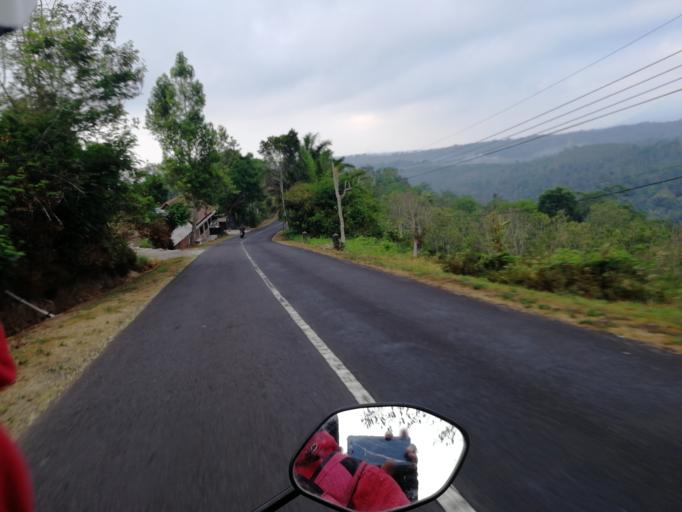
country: ID
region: Bali
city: Banjar Taro Kelod
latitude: -8.2558
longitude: 115.2452
